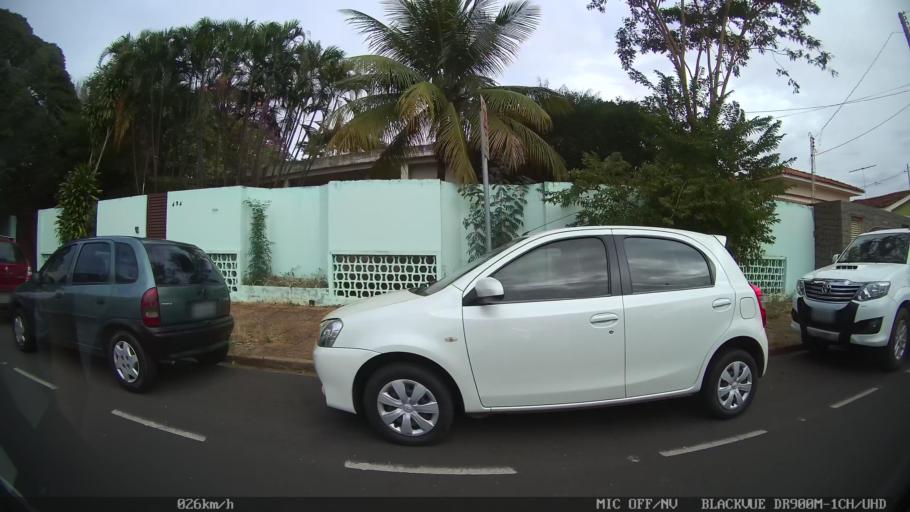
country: BR
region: Sao Paulo
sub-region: Sao Jose Do Rio Preto
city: Sao Jose do Rio Preto
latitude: -20.8213
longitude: -49.3710
